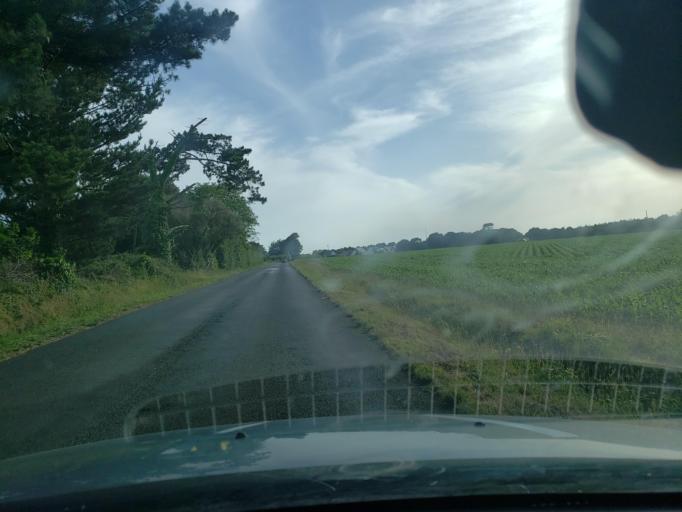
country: FR
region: Brittany
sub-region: Departement du Finistere
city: Treffiagat
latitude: 47.8101
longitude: -4.2503
